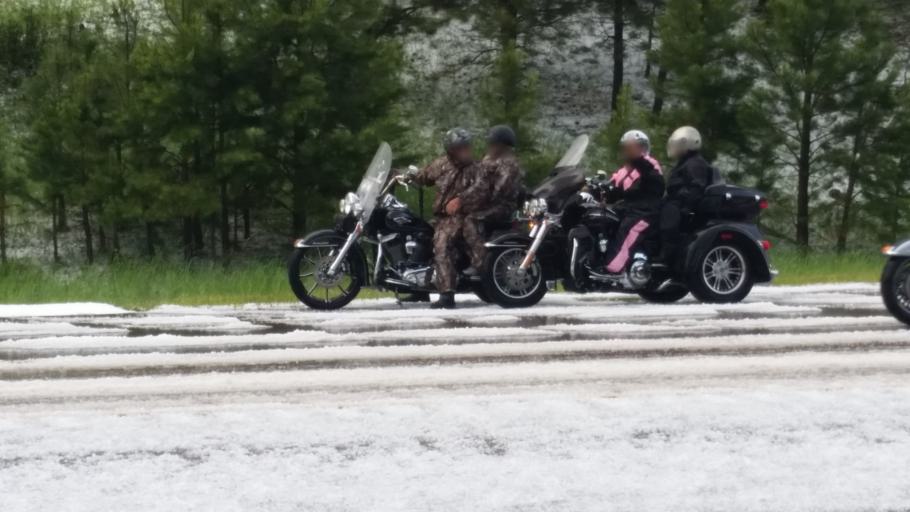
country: US
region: South Dakota
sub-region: Pennington County
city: Colonial Pine Hills
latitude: 43.9396
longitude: -103.4115
